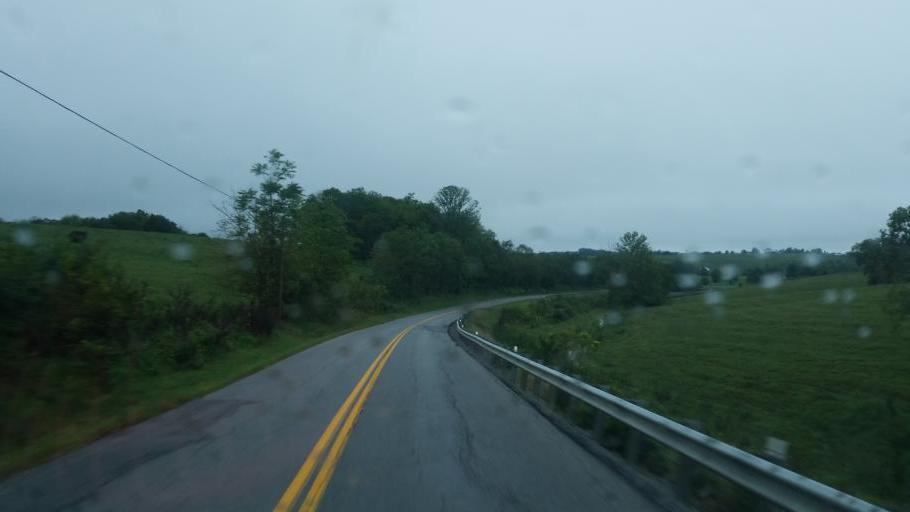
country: US
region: Kentucky
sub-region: Fleming County
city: Flemingsburg
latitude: 38.4135
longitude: -83.6860
